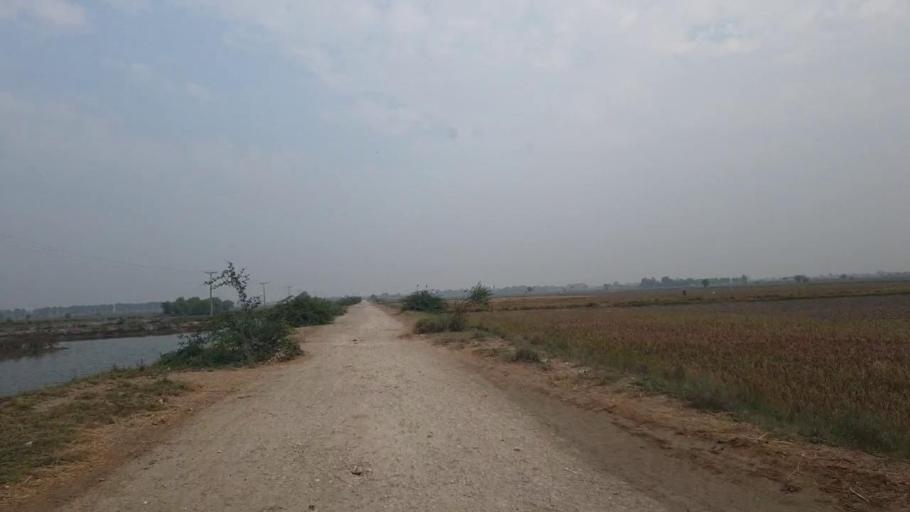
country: PK
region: Sindh
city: Talhar
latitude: 24.8167
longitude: 68.8768
